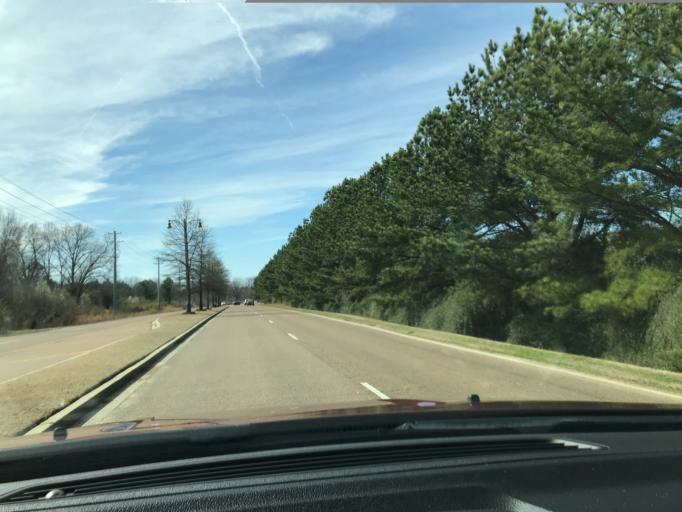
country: US
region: Tennessee
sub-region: Shelby County
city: Collierville
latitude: 35.0411
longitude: -89.7175
